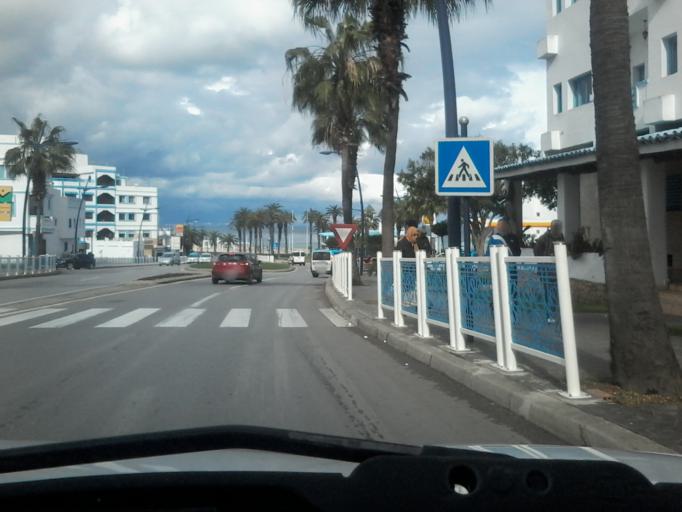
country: MA
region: Tanger-Tetouan
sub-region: Tetouan
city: Martil
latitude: 35.6814
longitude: -5.3210
